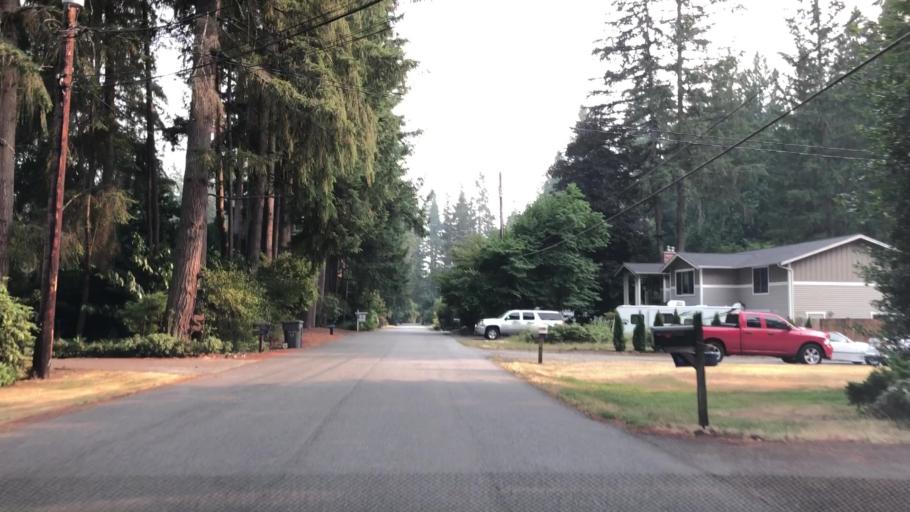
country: US
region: Washington
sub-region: King County
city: Cottage Lake
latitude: 47.7535
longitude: -122.0924
